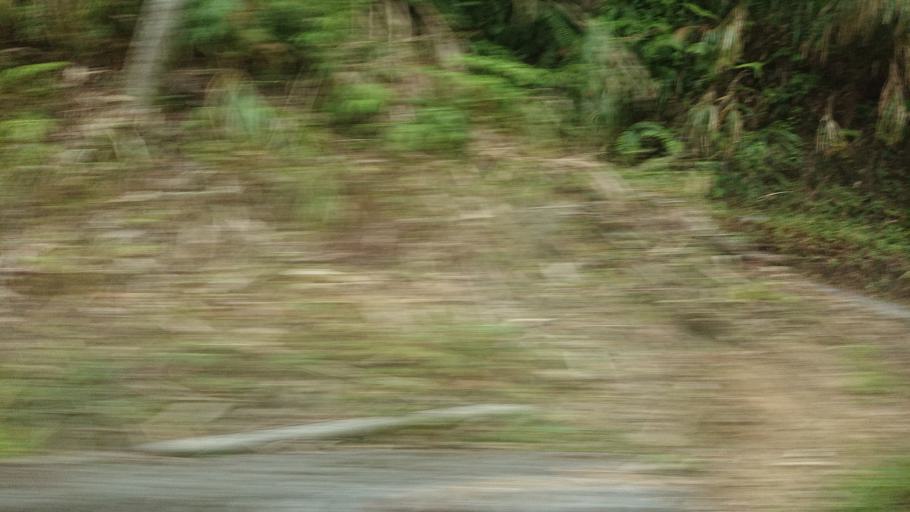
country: TW
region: Taiwan
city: Lugu
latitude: 23.6172
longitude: 120.7207
